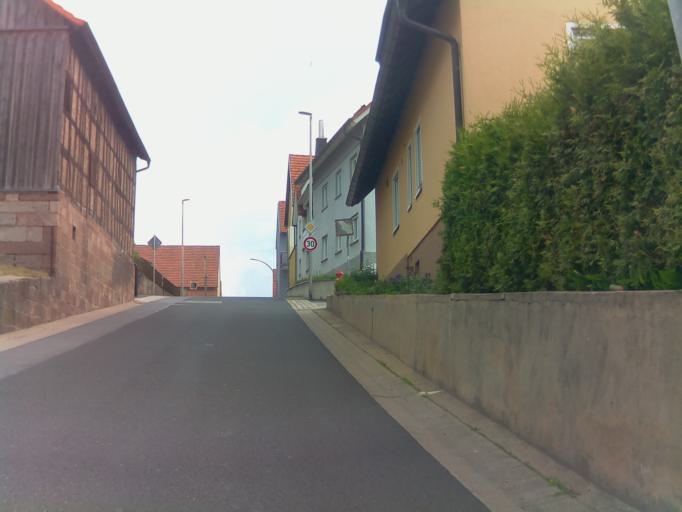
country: DE
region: Bavaria
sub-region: Regierungsbezirk Unterfranken
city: Burkardroth
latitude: 50.2855
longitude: 9.9847
